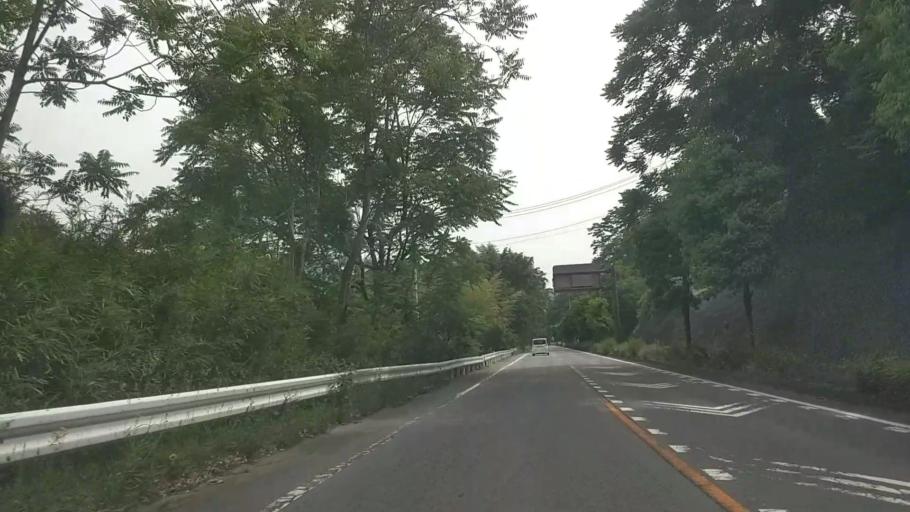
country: JP
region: Yamanashi
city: Isawa
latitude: 35.5918
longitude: 138.5900
